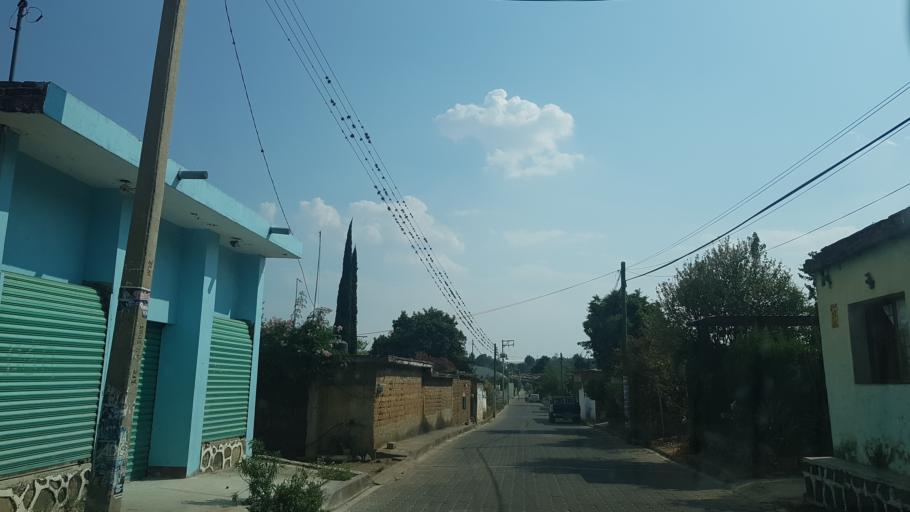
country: MX
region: Puebla
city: San Juan Amecac
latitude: 18.8220
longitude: -98.7050
